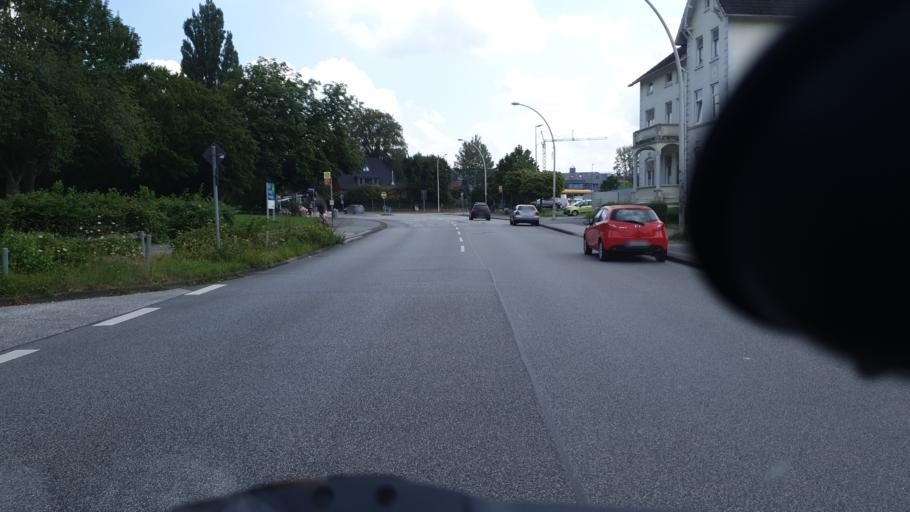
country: DE
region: Schleswig-Holstein
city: Kiel
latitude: 54.3509
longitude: 10.1248
